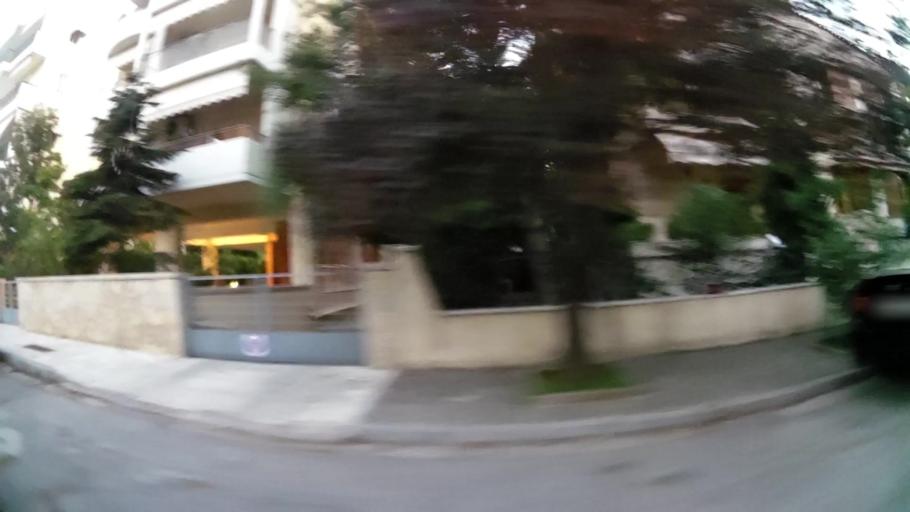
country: GR
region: Attica
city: Pefki
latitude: 38.0647
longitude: 23.8018
